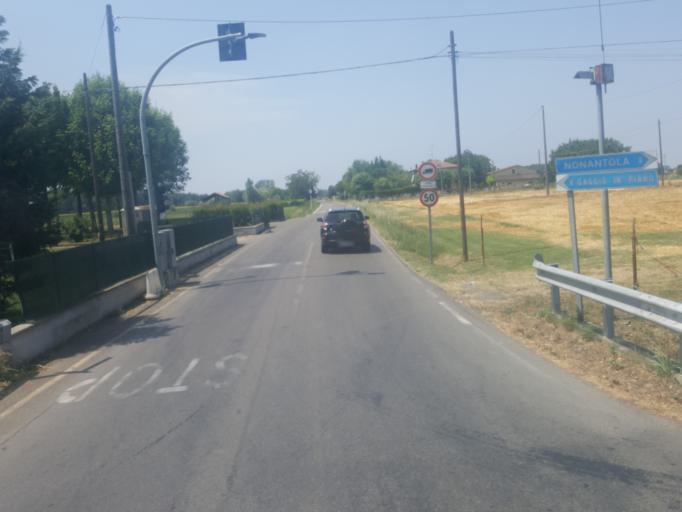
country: IT
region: Emilia-Romagna
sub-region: Provincia di Modena
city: Castelfranco Emilia
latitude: 44.6207
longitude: 11.0525
